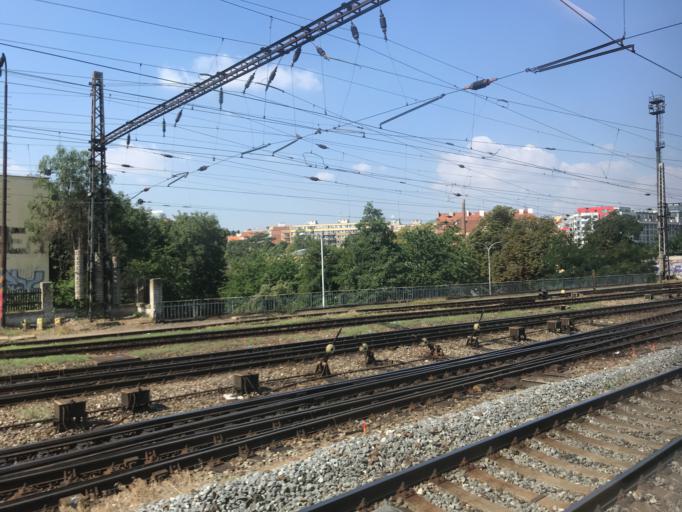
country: CZ
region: Praha
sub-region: Praha 8
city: Karlin
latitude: 50.0625
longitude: 14.4554
